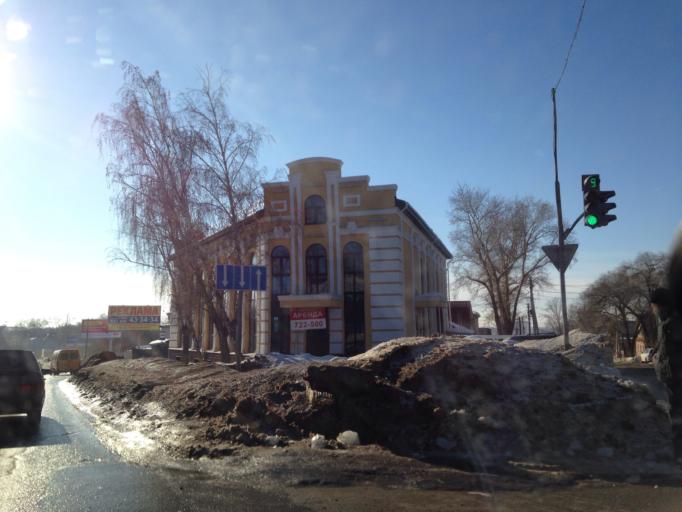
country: RU
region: Ulyanovsk
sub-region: Ulyanovskiy Rayon
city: Ulyanovsk
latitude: 54.3150
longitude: 48.3807
